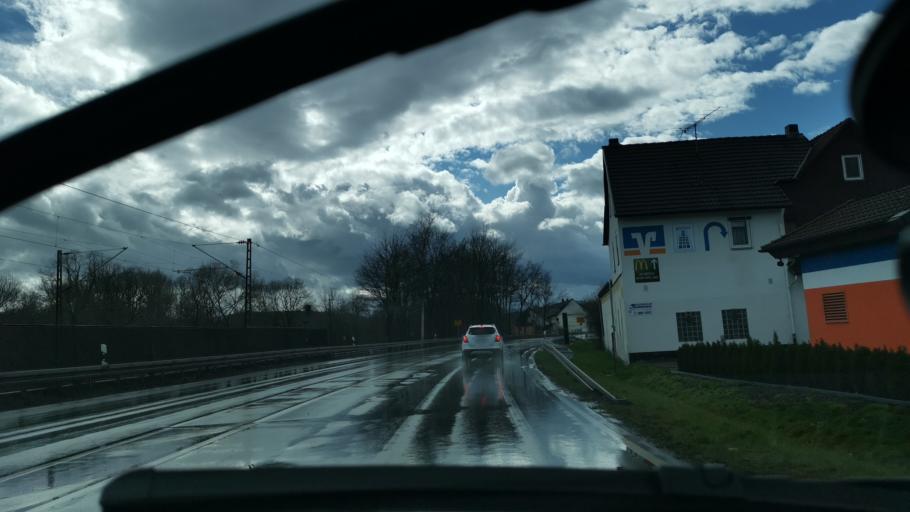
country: DE
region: Hesse
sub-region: Regierungsbezirk Kassel
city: Bad Hersfeld
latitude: 50.8994
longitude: 9.7468
